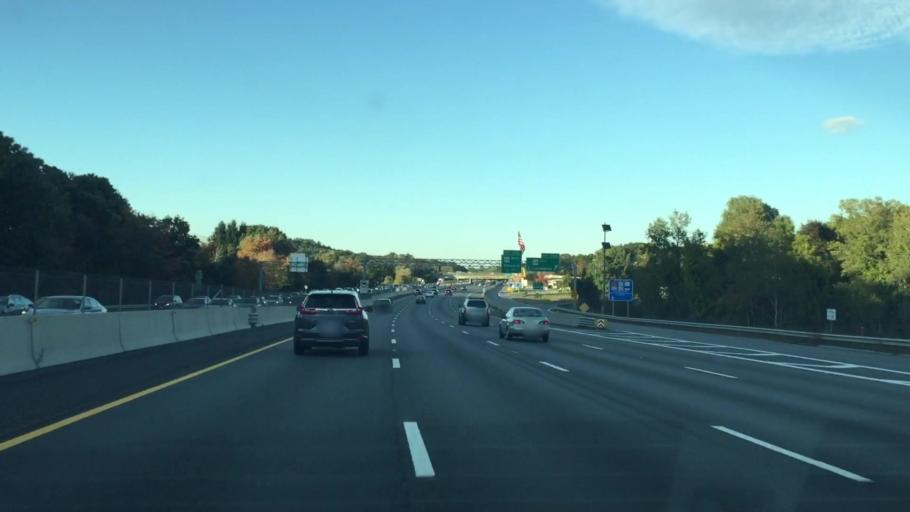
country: US
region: Massachusetts
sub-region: Middlesex County
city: Lexington
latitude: 42.4368
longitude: -71.2594
